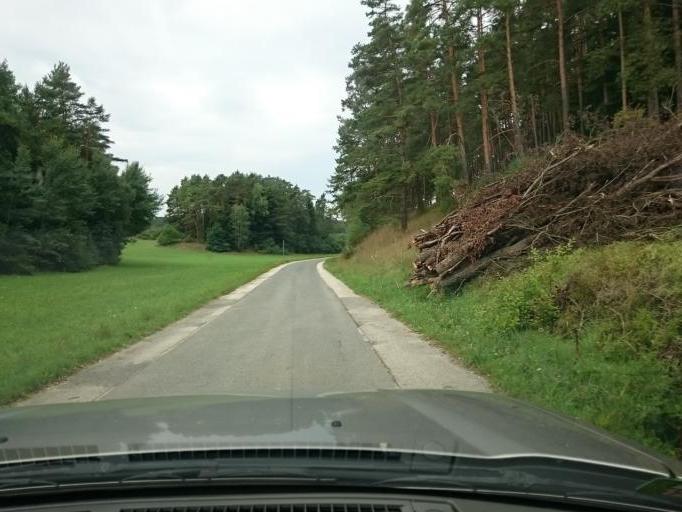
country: DE
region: Bavaria
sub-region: Regierungsbezirk Mittelfranken
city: Velden
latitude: 49.6592
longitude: 11.4688
